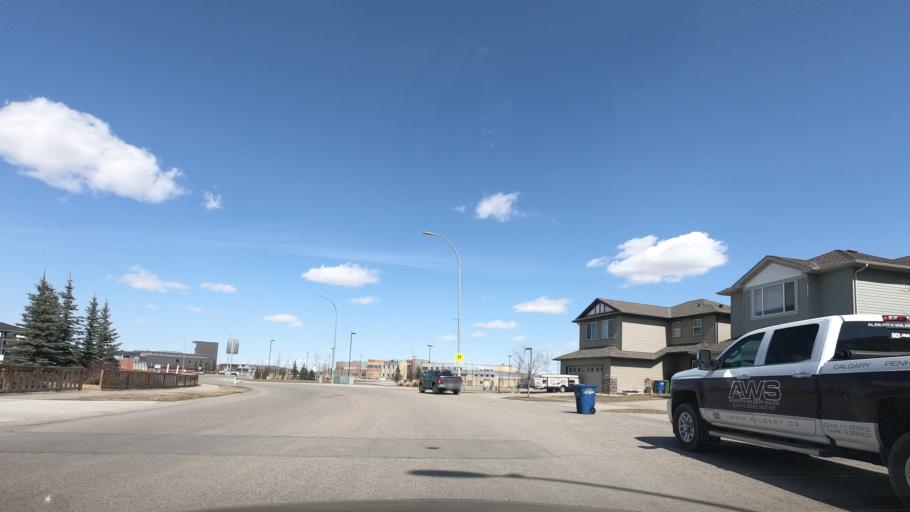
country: CA
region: Alberta
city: Airdrie
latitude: 51.2677
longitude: -114.0298
